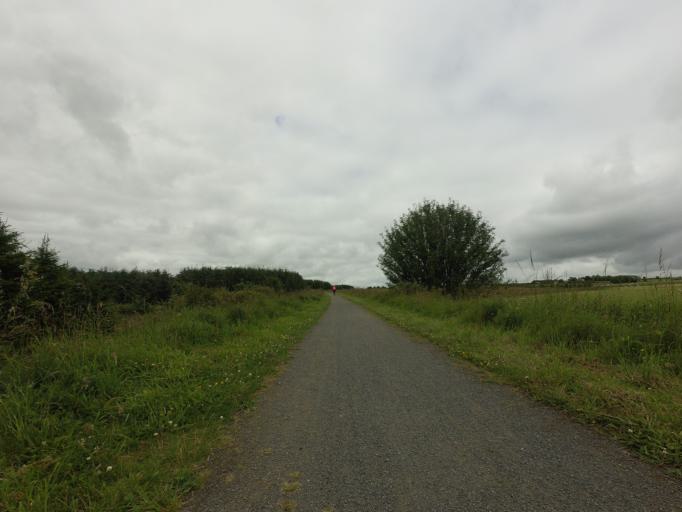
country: GB
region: Scotland
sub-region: Aberdeenshire
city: Mintlaw
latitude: 57.4937
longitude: -2.1367
